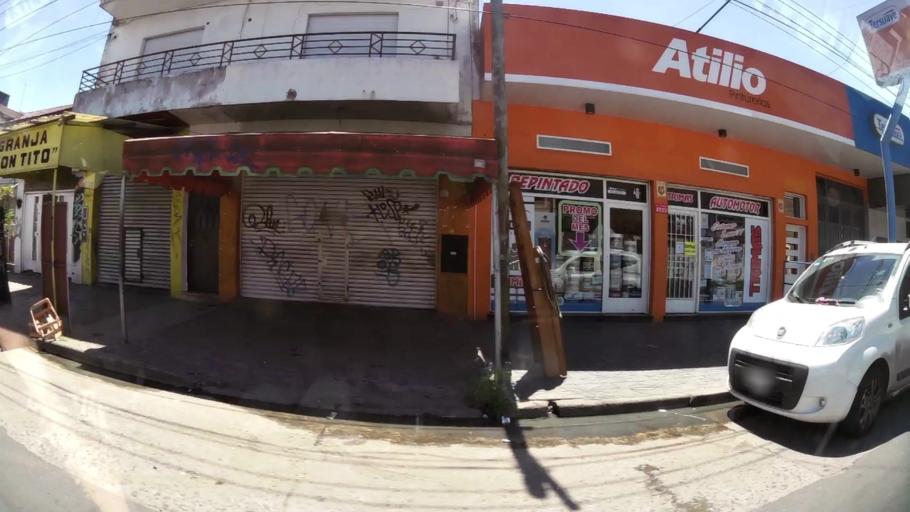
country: AR
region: Buenos Aires
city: Caseros
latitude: -34.5904
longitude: -58.5580
